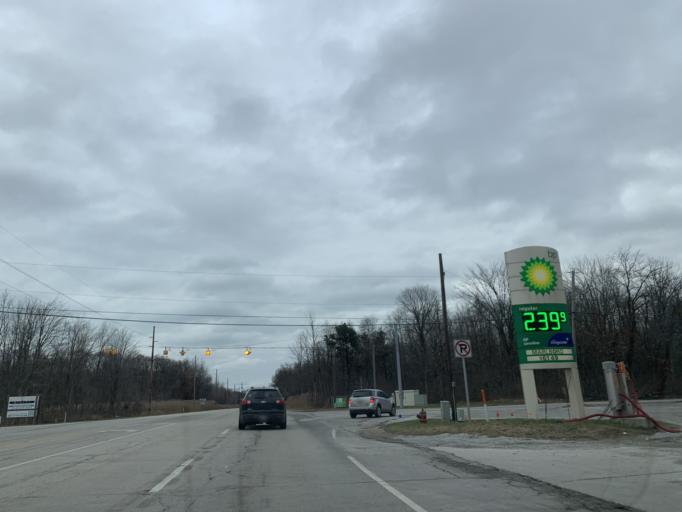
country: US
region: Indiana
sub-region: LaPorte County
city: Long Beach
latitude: 41.7232
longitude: -86.8260
